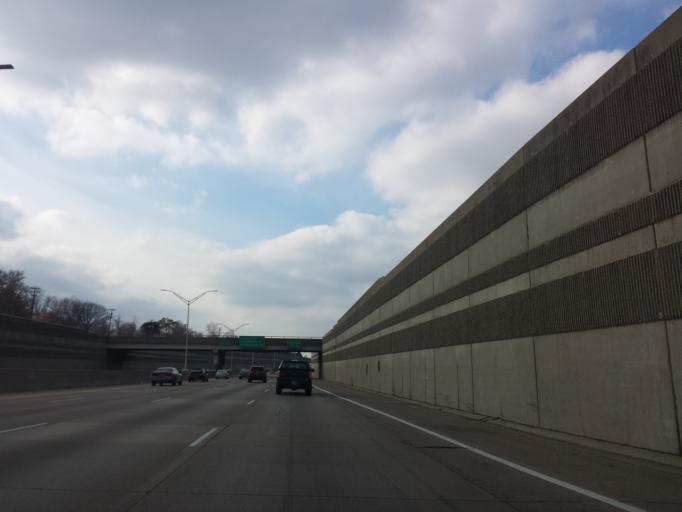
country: US
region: Michigan
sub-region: Oakland County
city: Huntington Woods
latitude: 42.4746
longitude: -83.1585
